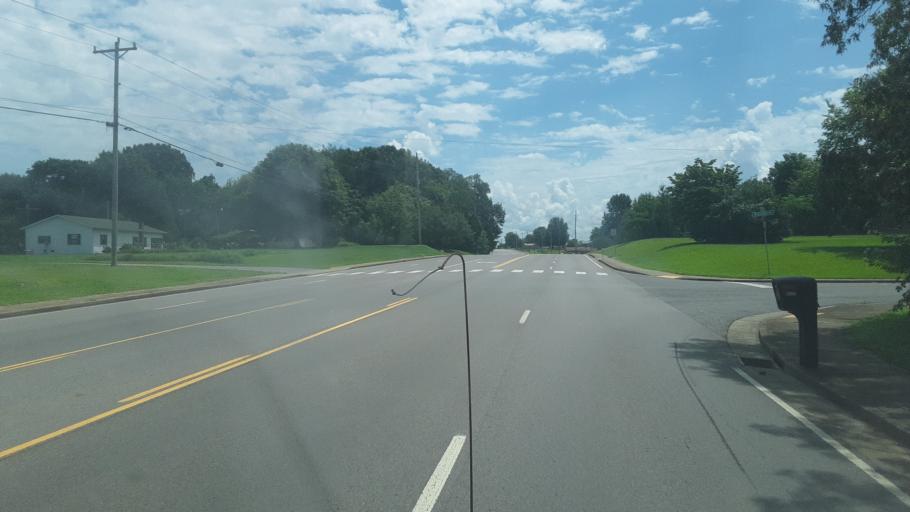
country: US
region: Kentucky
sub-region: Christian County
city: Fort Campbell North
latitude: 36.5761
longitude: -87.4437
